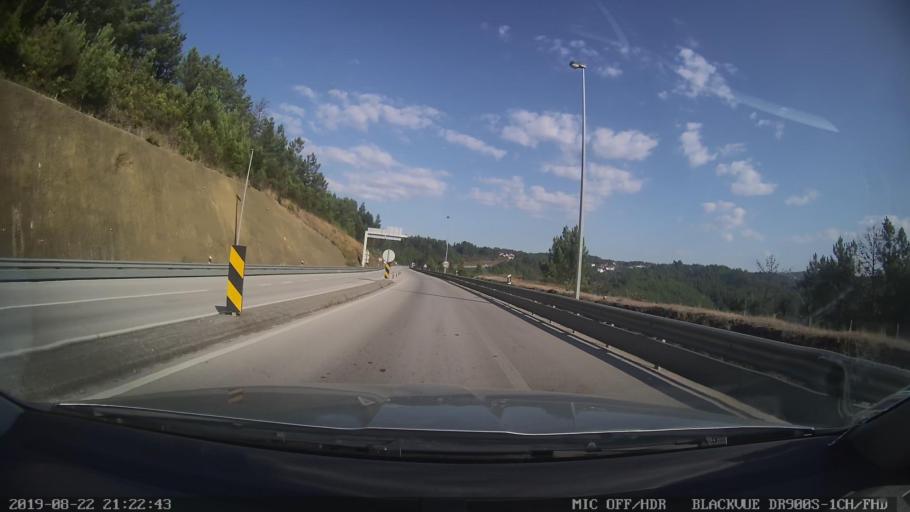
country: PT
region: Castelo Branco
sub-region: Serta
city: Serta
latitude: 39.8224
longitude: -8.1028
